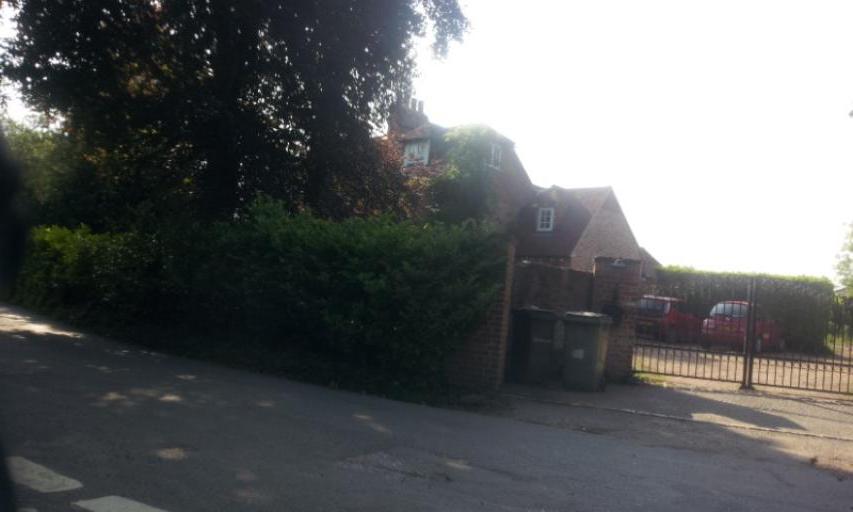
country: GB
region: England
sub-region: Kent
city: Harrietsham
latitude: 51.2450
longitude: 0.6586
